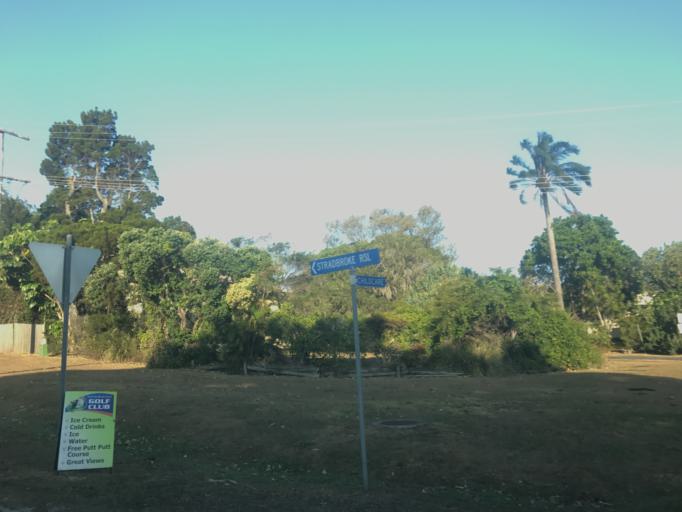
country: AU
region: Queensland
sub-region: Redland
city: Victoria Point
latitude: -27.5007
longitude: 153.4039
